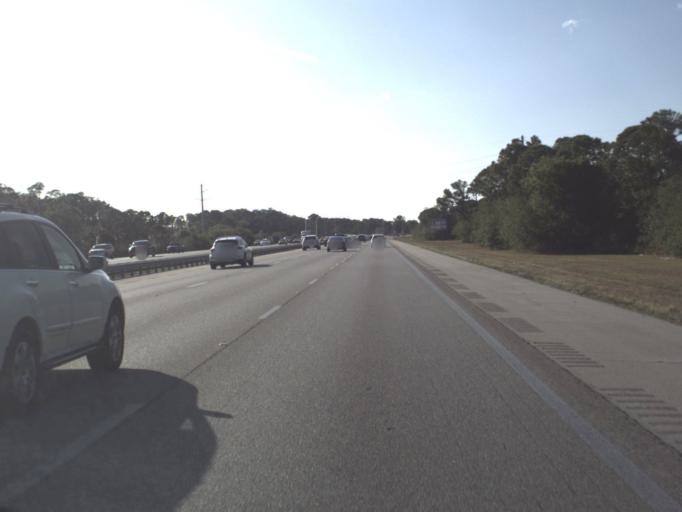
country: US
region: Florida
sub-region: Brevard County
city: June Park
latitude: 28.0665
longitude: -80.6981
